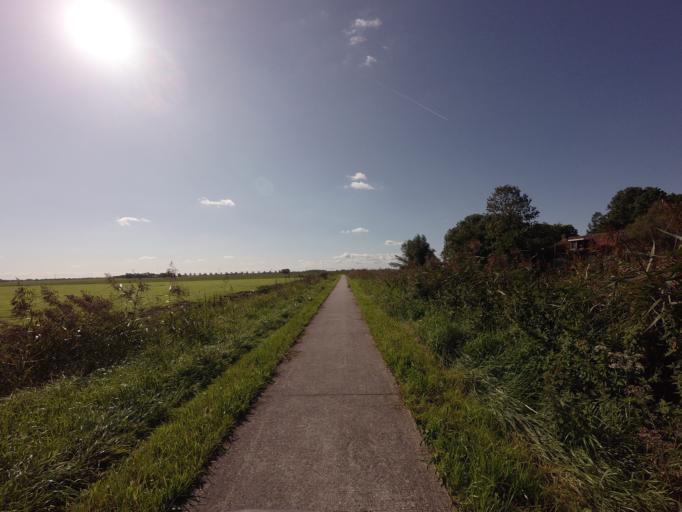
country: NL
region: Friesland
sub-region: Gemeente Boarnsterhim
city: Reduzum
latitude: 53.1289
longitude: 5.7557
